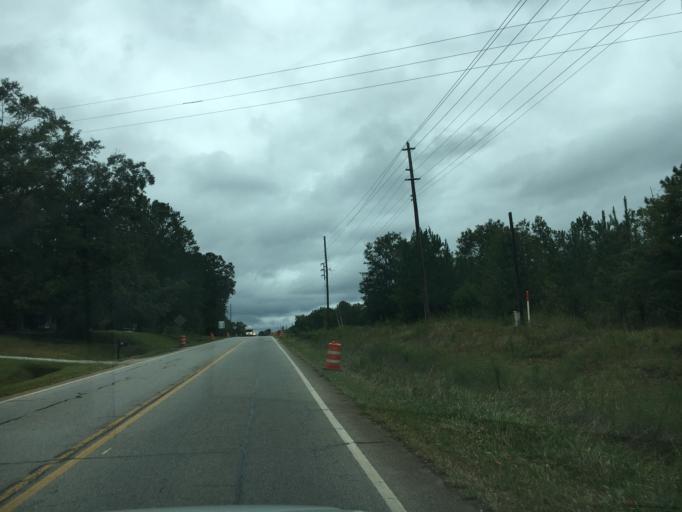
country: US
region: Georgia
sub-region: Wilkes County
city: Washington
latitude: 33.6947
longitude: -82.6813
